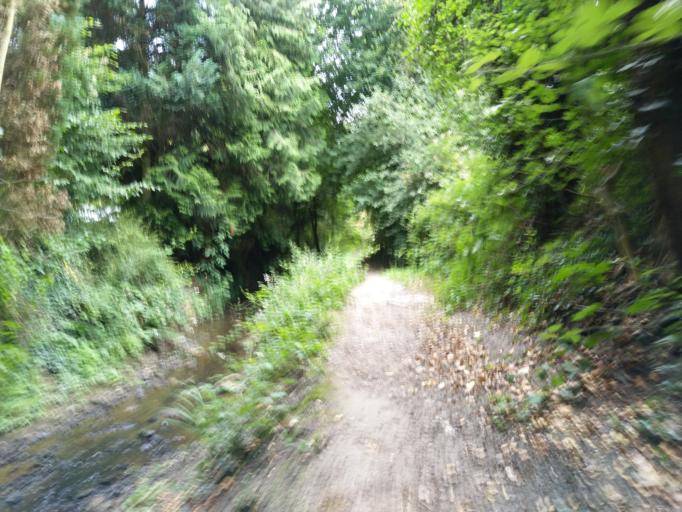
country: BE
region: Wallonia
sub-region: Province du Hainaut
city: Roeulx
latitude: 50.4901
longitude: 4.0604
